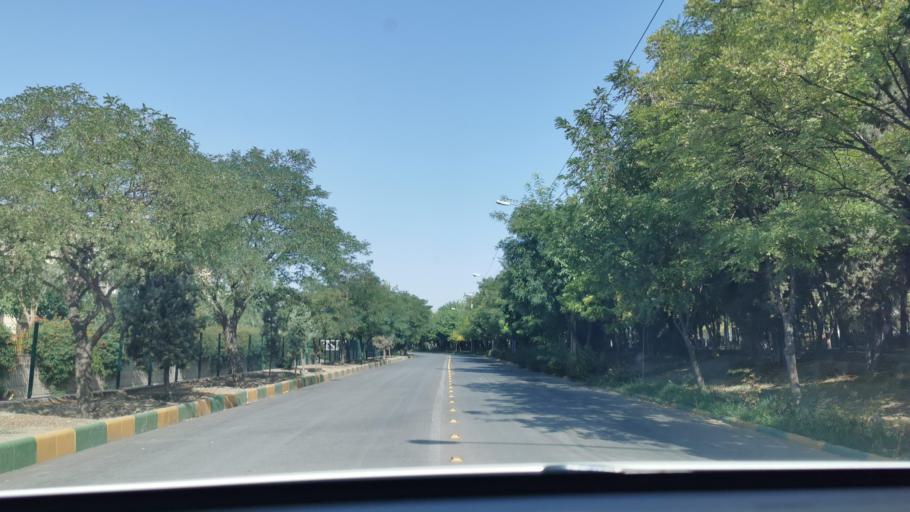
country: IR
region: Razavi Khorasan
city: Mashhad
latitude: 36.3296
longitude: 59.6356
